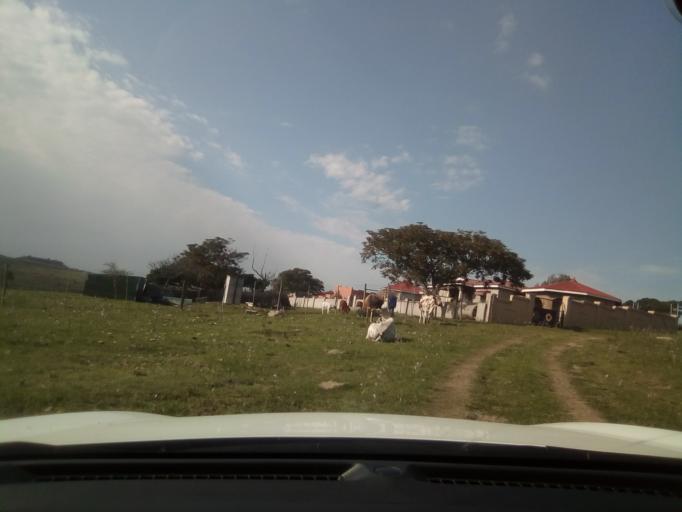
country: ZA
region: Eastern Cape
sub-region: Buffalo City Metropolitan Municipality
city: Bhisho
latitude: -32.9814
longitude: 27.2581
